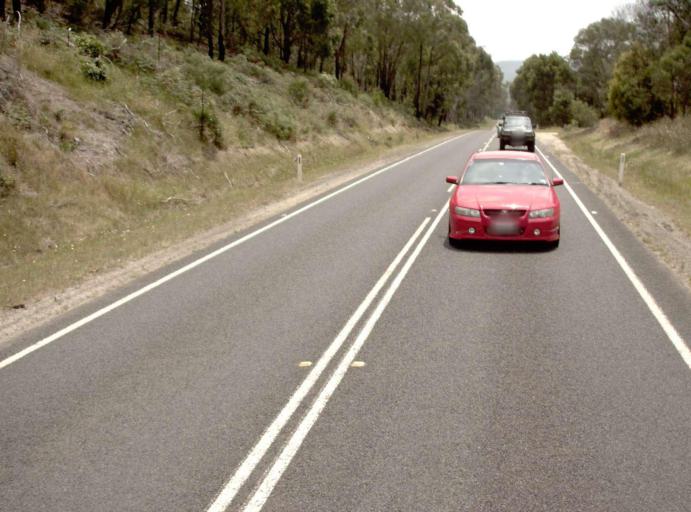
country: AU
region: Victoria
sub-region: Latrobe
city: Traralgon
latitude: -38.4485
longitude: 146.7359
